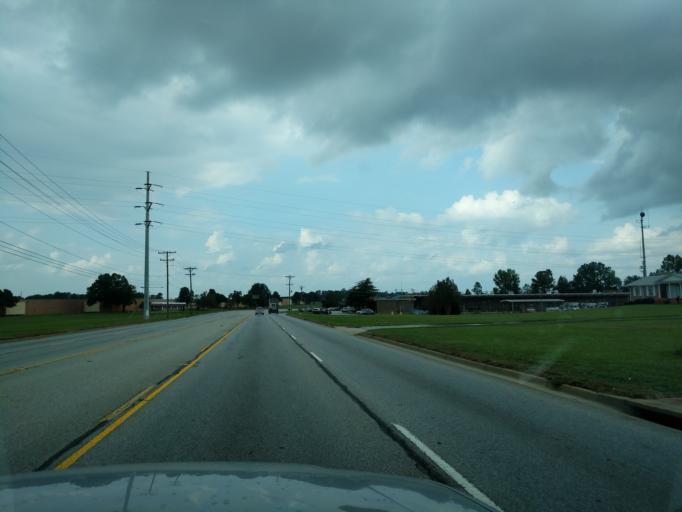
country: US
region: South Carolina
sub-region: Anderson County
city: Centerville
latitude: 34.5395
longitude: -82.6997
